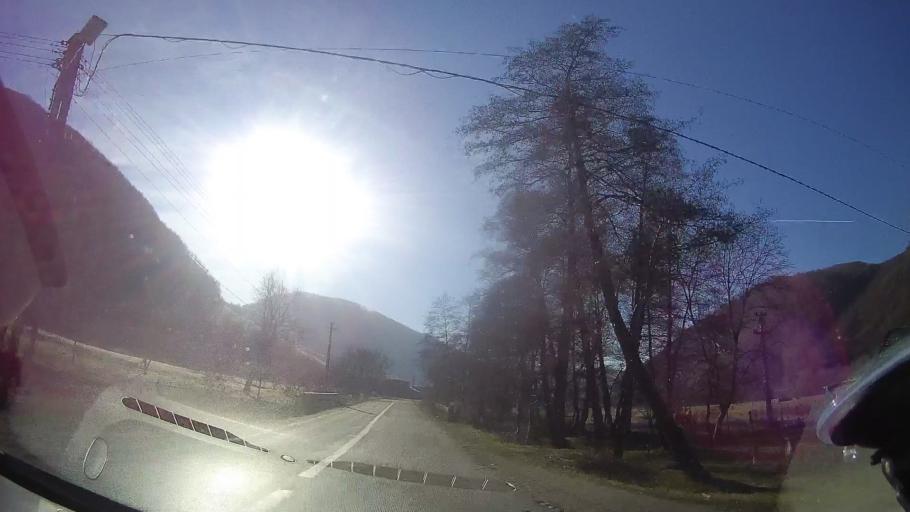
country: RO
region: Bihor
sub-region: Comuna Bulz
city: Bulz
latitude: 46.9462
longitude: 22.6749
